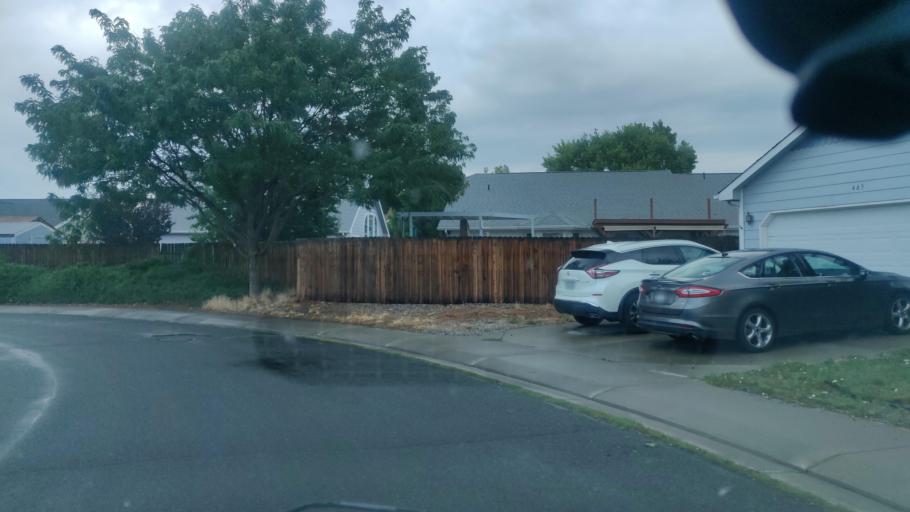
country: US
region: Colorado
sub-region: Mesa County
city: Fruitvale
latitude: 39.0734
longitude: -108.4848
